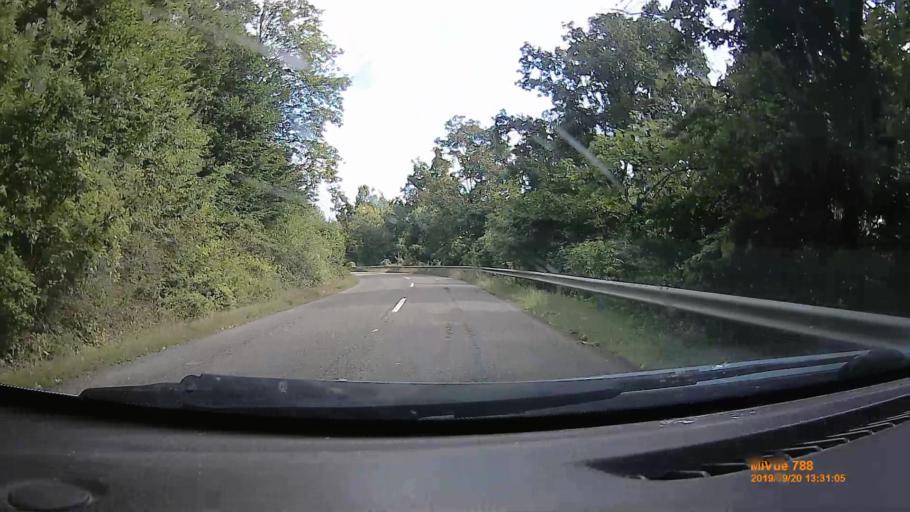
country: HU
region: Heves
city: Szilvasvarad
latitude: 48.0539
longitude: 20.4897
